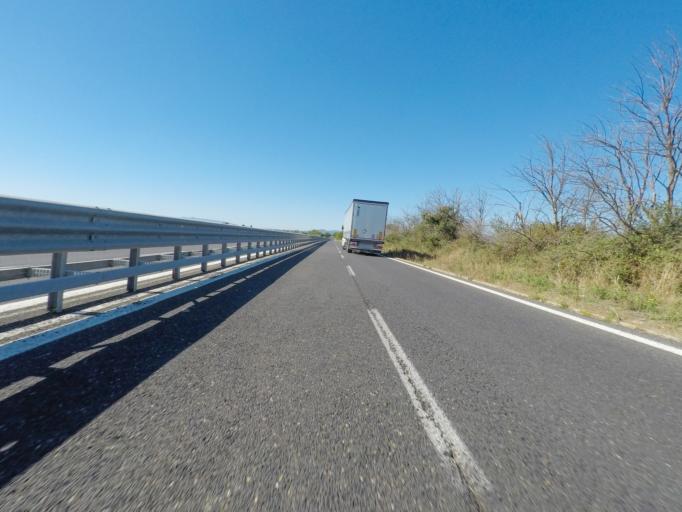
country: IT
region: Latium
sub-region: Provincia di Viterbo
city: Pescia Romana
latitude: 42.3915
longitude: 11.5379
